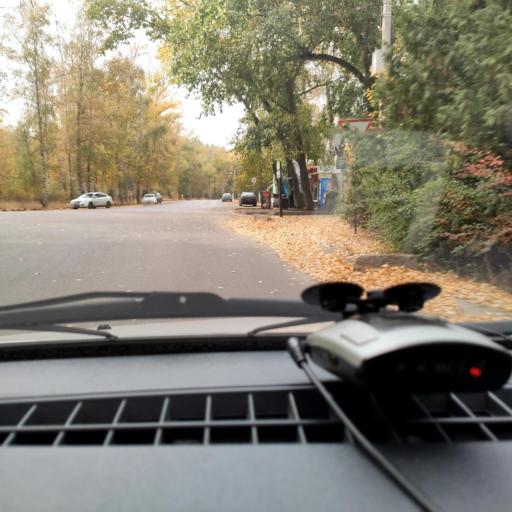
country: RU
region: Voronezj
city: Podgornoye
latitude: 51.7420
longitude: 39.1725
